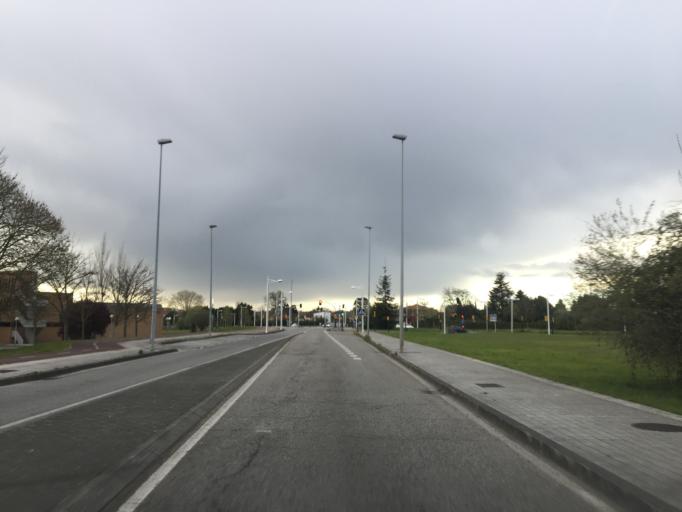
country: ES
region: Asturias
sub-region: Province of Asturias
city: Gijon
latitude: 43.5263
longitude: -5.6268
